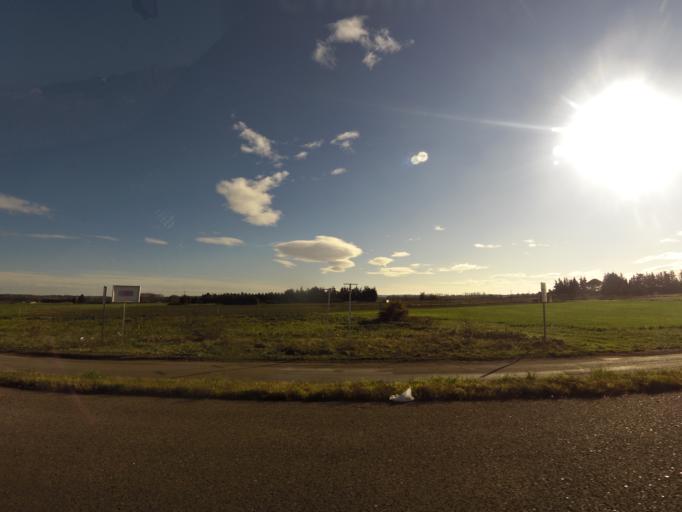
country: FR
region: Languedoc-Roussillon
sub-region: Departement du Gard
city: Milhaud
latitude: 43.7818
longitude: 4.3079
